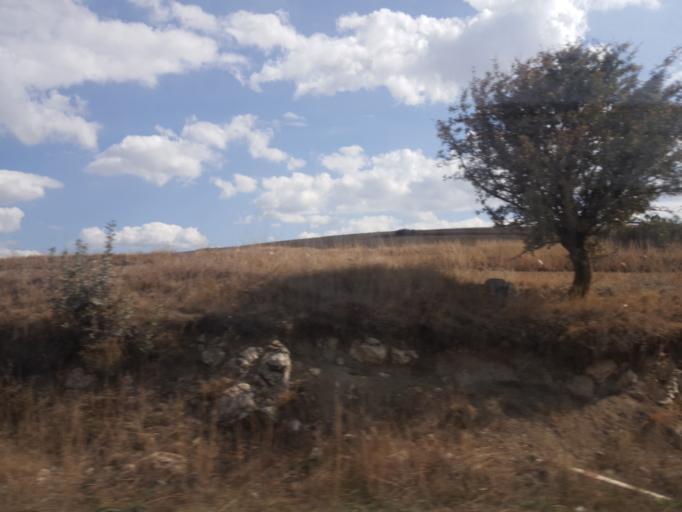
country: TR
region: Tokat
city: Artova
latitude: 40.1215
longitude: 36.3166
